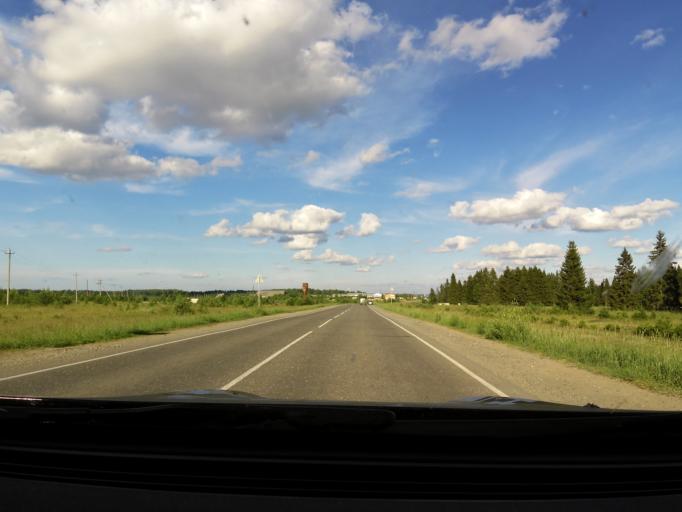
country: RU
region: Kirov
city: Omutninsk
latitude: 58.6891
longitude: 52.1713
